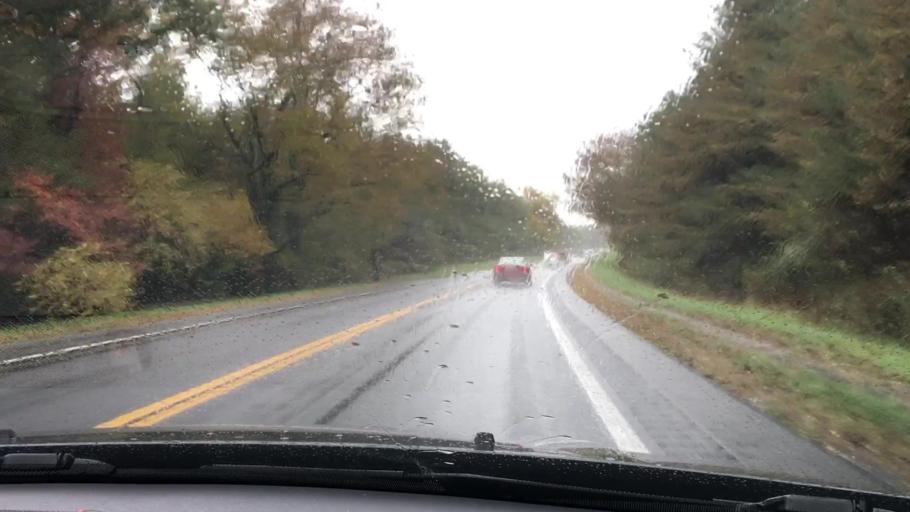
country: US
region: Virginia
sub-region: Loudoun County
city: Leesburg
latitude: 39.1636
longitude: -77.5362
